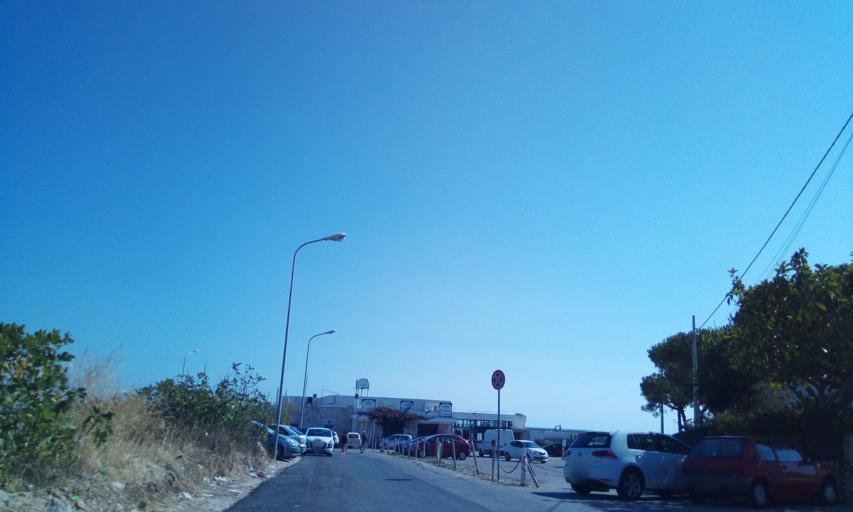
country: IT
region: Apulia
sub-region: Provincia di Bari
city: Polignano a Mare
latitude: 41.0034
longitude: 17.2006
